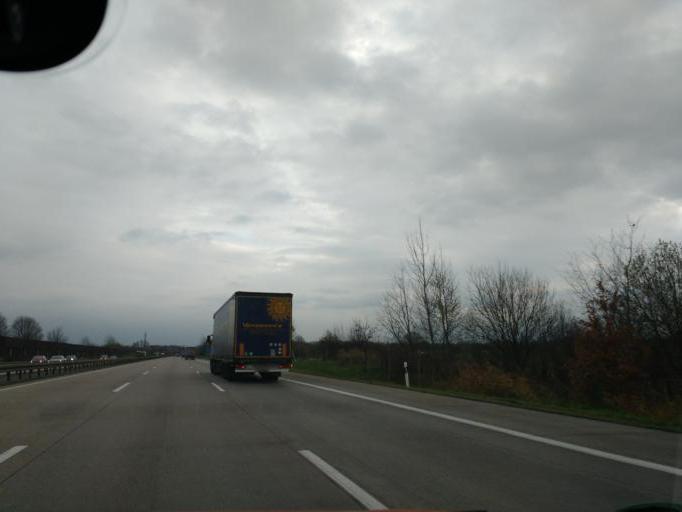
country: DE
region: Lower Saxony
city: Isernhagen Farster Bauerschaft
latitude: 52.4869
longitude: 9.8415
